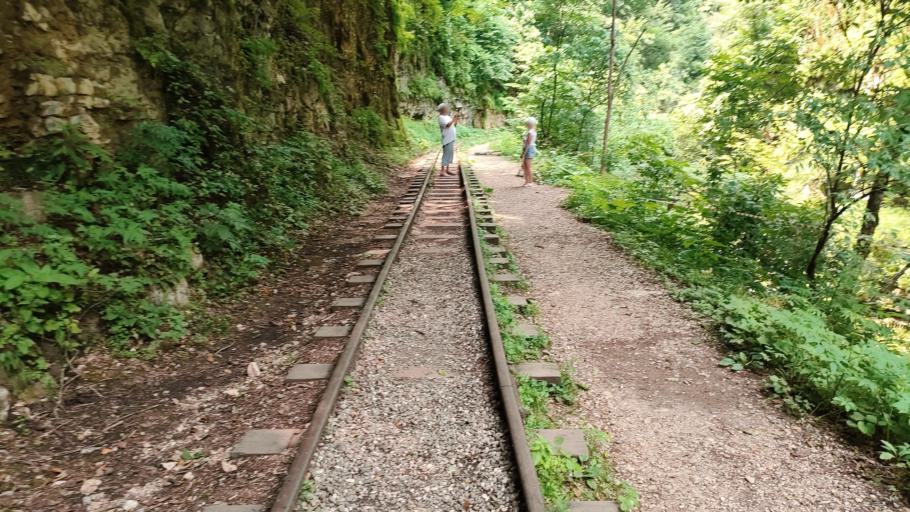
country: RU
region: Krasnodarskiy
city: Neftegorsk
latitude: 44.2096
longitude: 39.9077
